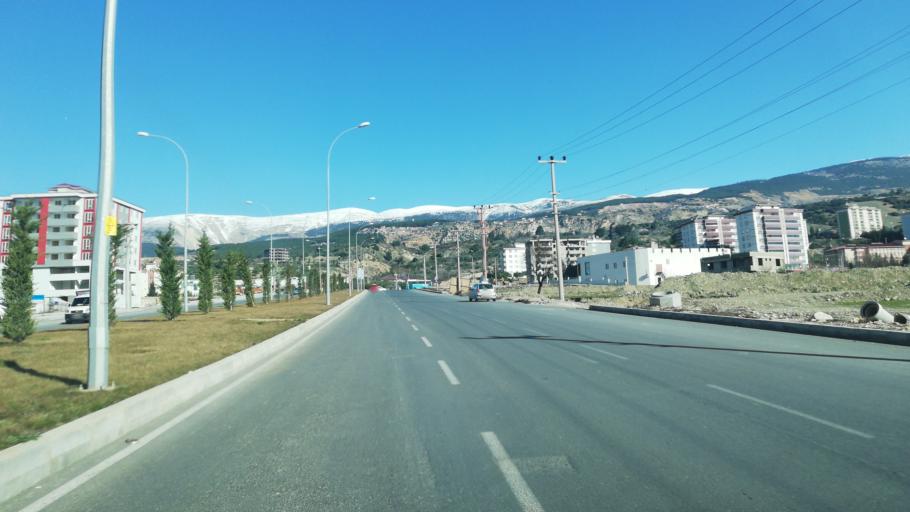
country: TR
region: Kahramanmaras
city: Kahramanmaras
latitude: 37.5803
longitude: 36.9747
